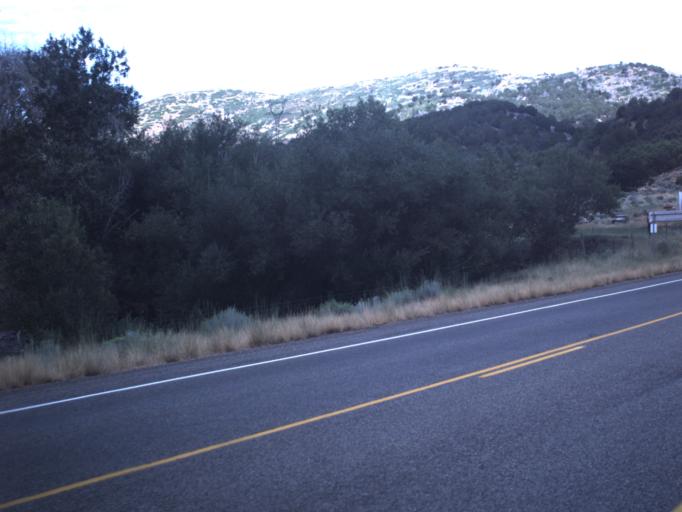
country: US
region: Utah
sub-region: Juab County
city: Nephi
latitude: 39.7180
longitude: -111.7293
